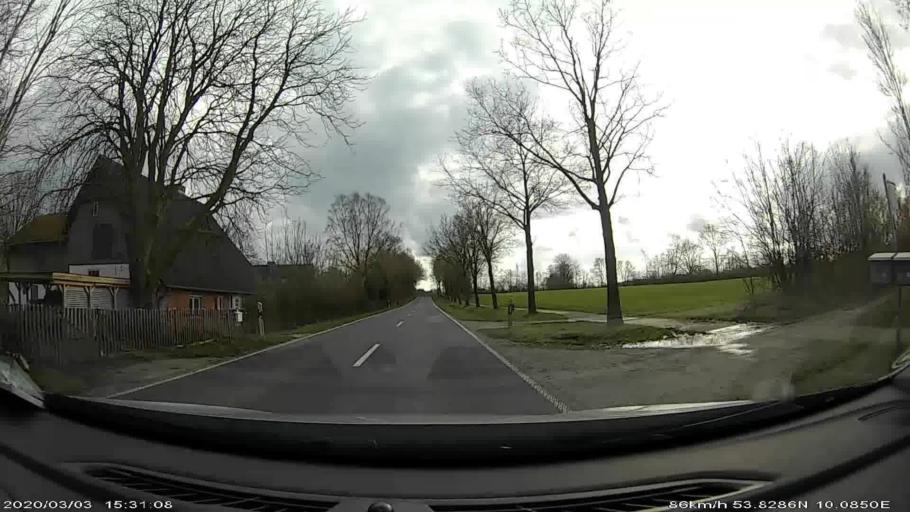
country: DE
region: Schleswig-Holstein
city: Huttblek
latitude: 53.8296
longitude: 10.0855
